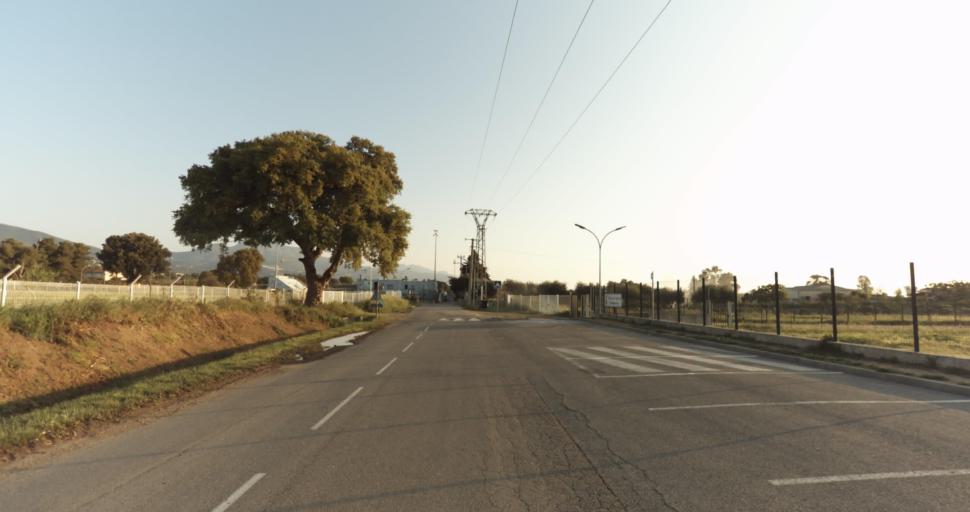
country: FR
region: Corsica
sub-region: Departement de la Haute-Corse
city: Biguglia
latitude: 42.6186
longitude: 9.4433
